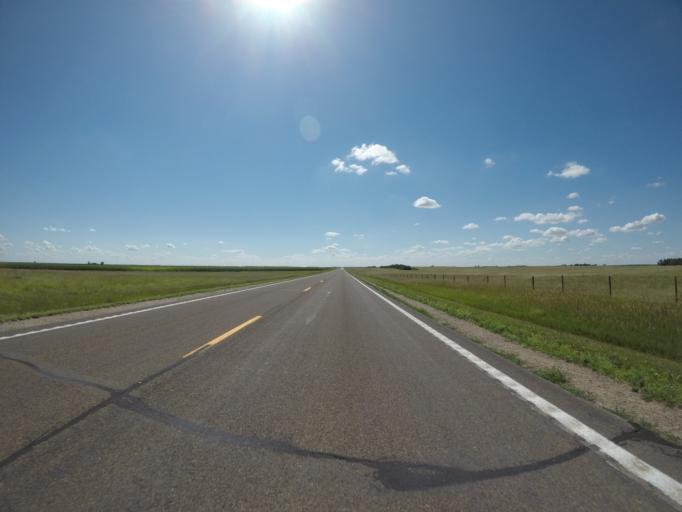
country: US
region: Nebraska
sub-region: Chase County
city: Imperial
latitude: 40.5376
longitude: -101.8566
